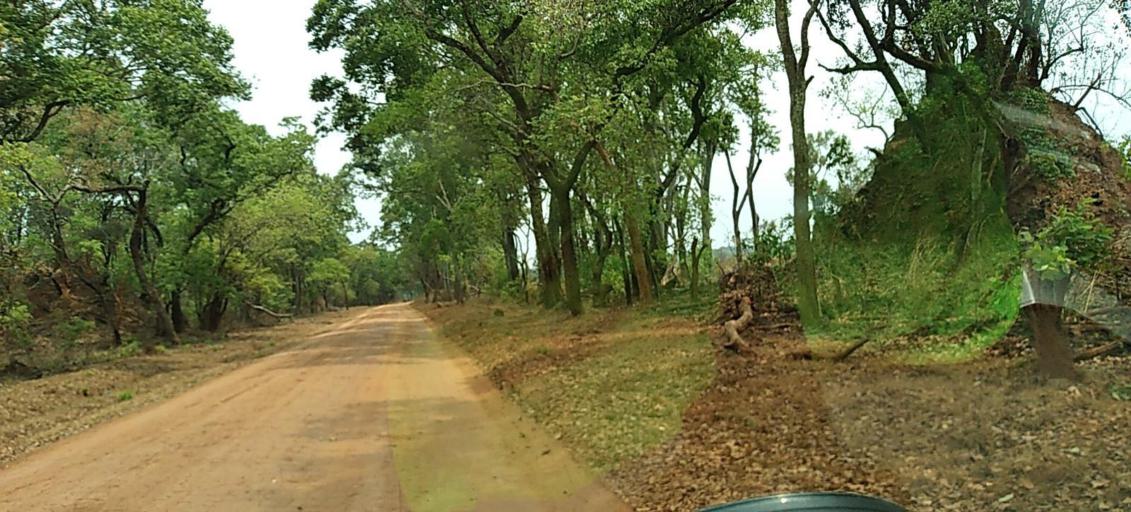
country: ZM
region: North-Western
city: Solwezi
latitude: -12.8125
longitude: 26.5367
